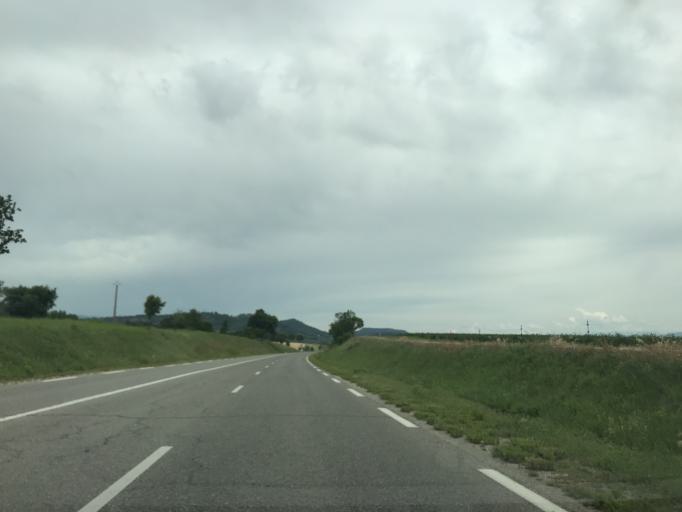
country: FR
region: Provence-Alpes-Cote d'Azur
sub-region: Departement des Alpes-de-Haute-Provence
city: Oraison
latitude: 43.9439
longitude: 5.8888
